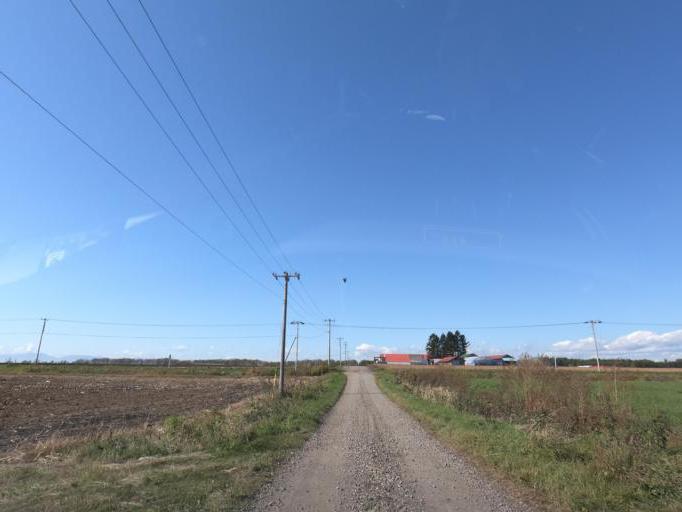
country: JP
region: Hokkaido
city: Otofuke
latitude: 43.0651
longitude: 143.2721
